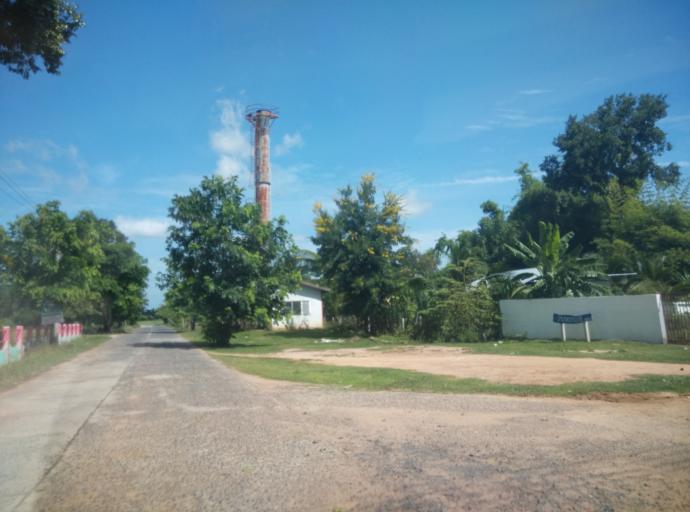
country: TH
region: Sisaket
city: Huai Thap Than
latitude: 14.9758
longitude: 104.0520
